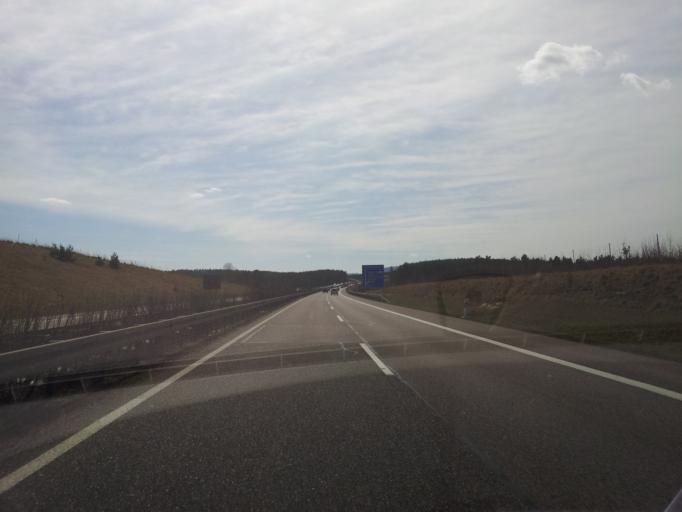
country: DE
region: Thuringia
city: Langewiesen
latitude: 50.7213
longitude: 10.9744
